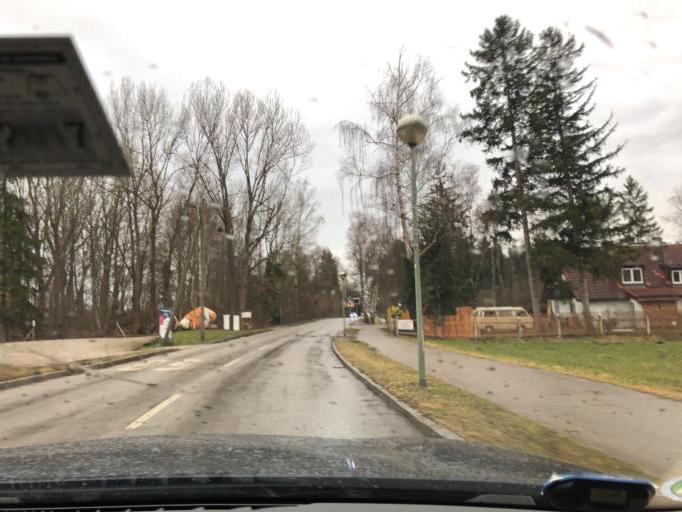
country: DE
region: Bavaria
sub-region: Upper Bavaria
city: Grobenzell
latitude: 48.2005
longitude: 11.3906
